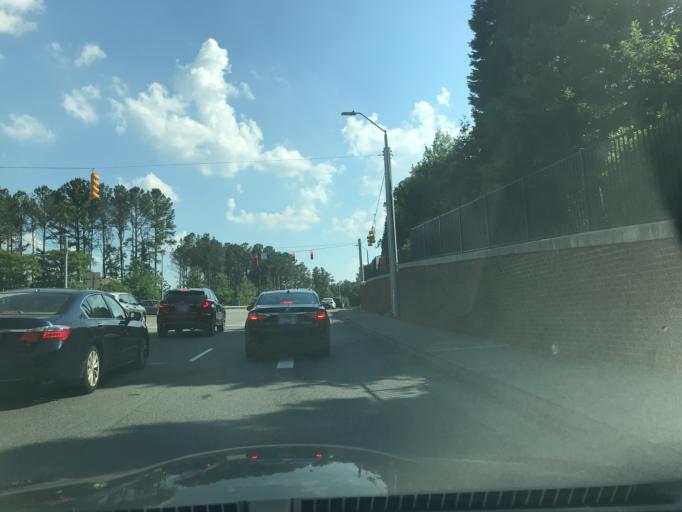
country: US
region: North Carolina
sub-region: Wake County
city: Wake Forest
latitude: 35.9264
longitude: -78.5877
